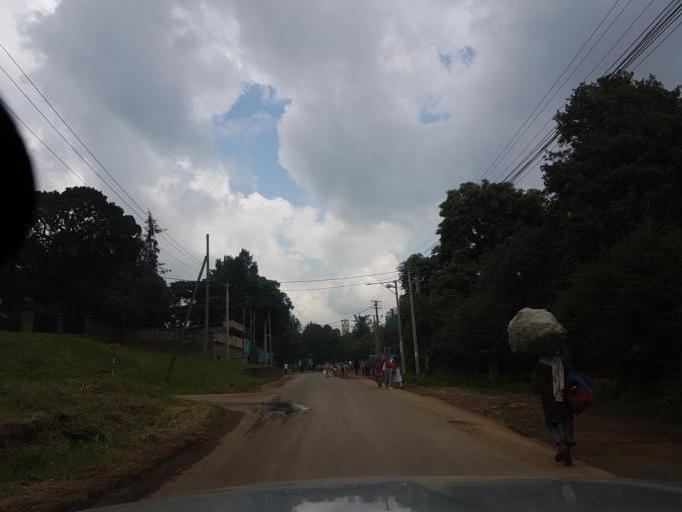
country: ET
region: Adis Abeba
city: Addis Ababa
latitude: 9.0260
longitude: 38.7669
